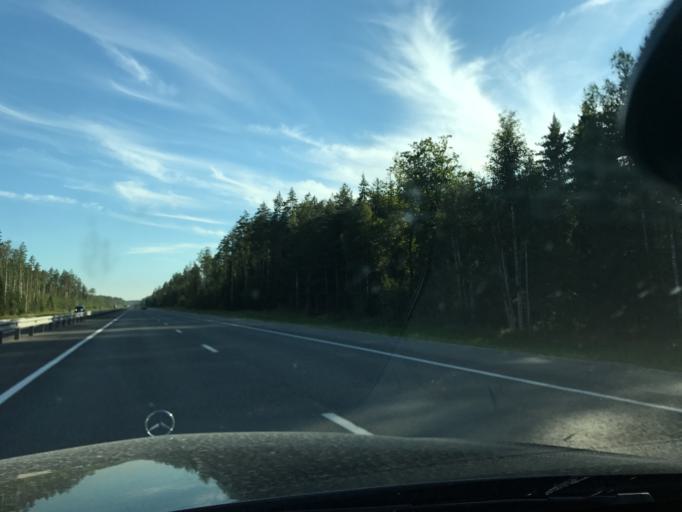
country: RU
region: Vladimir
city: Kameshkovo
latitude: 56.1712
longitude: 40.9402
